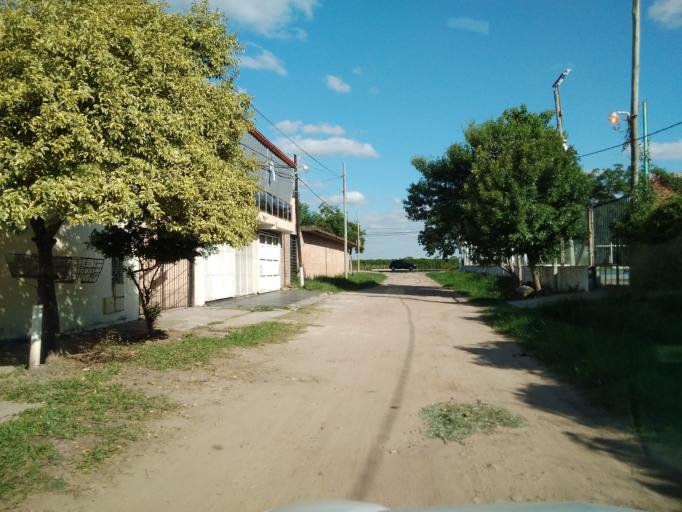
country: AR
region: Corrientes
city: Corrientes
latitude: -27.4624
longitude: -58.7757
